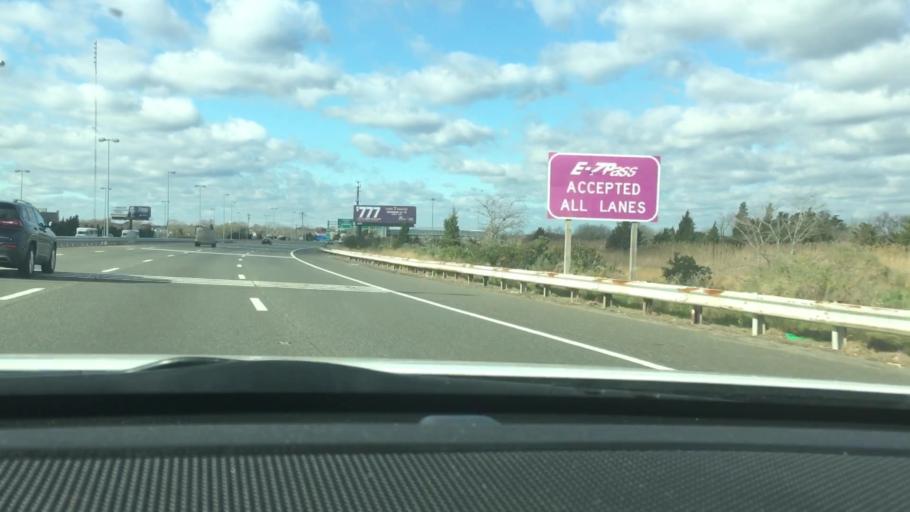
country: US
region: New Jersey
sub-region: Atlantic County
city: Pleasantville
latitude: 39.3871
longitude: -74.5062
